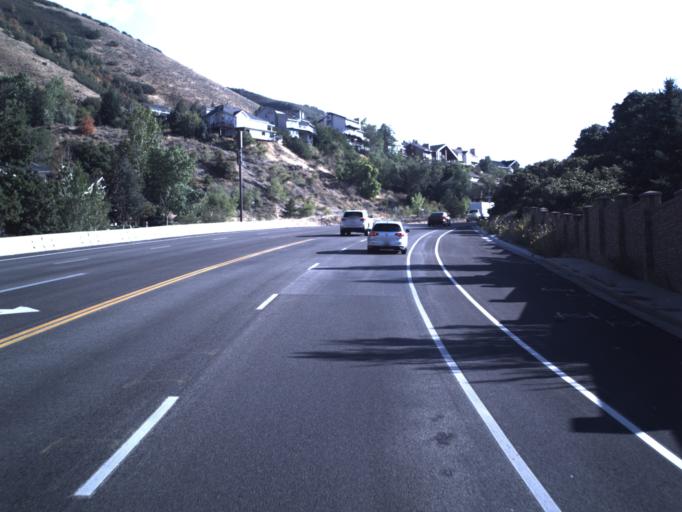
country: US
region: Utah
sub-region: Salt Lake County
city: Cottonwood Heights
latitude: 40.6159
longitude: -111.7888
